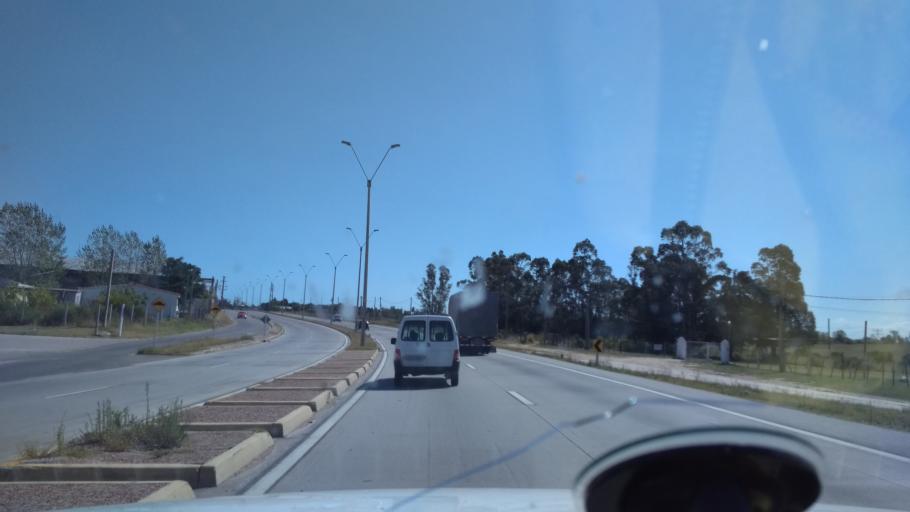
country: UY
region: Canelones
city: Toledo
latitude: -34.7904
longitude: -56.1100
